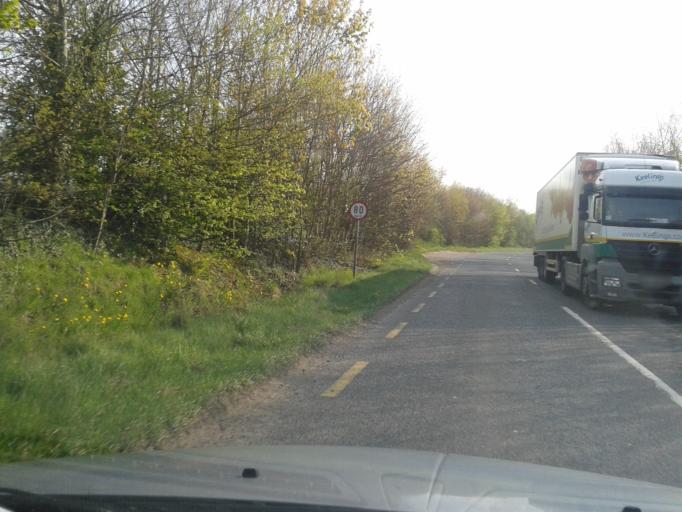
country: IE
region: Leinster
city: Ballymun
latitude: 53.4363
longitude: -6.2922
